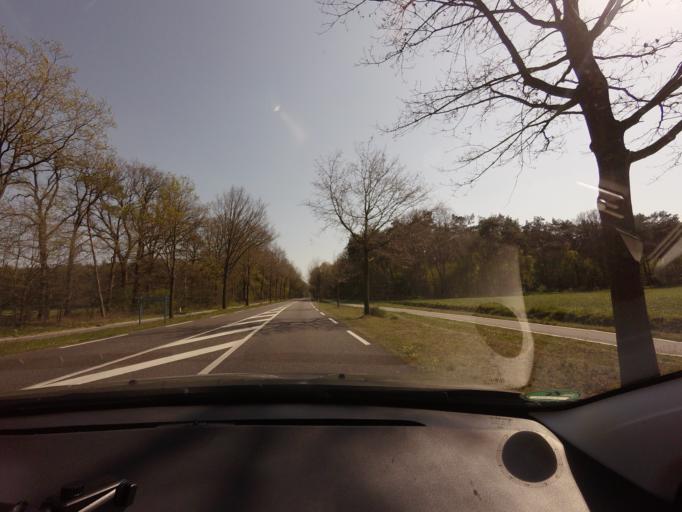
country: NL
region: North Brabant
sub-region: Gemeente Baarle-Nassau
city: Baarle-Nassau
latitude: 51.5085
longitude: 4.9635
